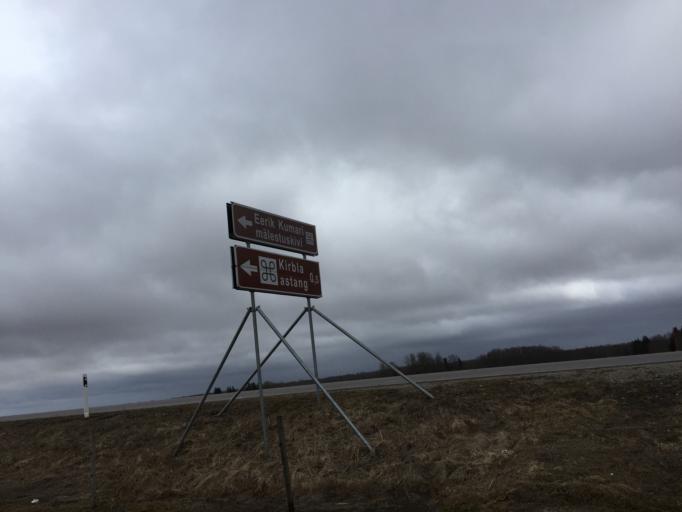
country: EE
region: Laeaene
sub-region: Lihula vald
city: Lihula
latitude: 58.7262
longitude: 23.9295
